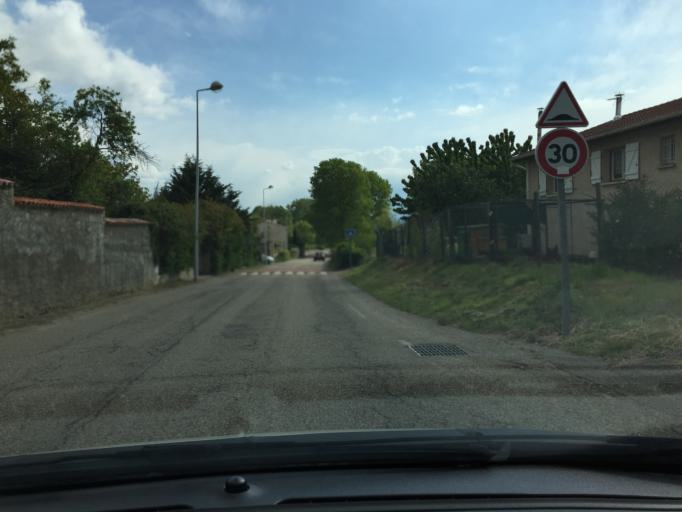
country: FR
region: Rhone-Alpes
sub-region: Departement du Rhone
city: Orlienas
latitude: 45.6443
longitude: 4.6916
